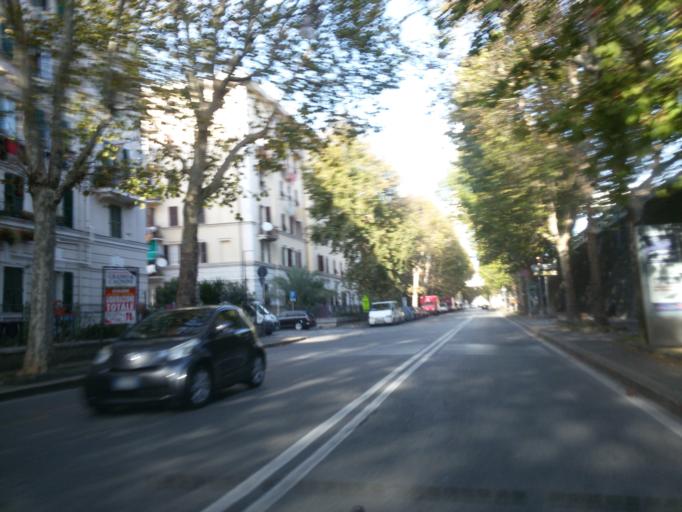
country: IT
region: Liguria
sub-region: Provincia di Genova
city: San Teodoro
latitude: 44.4230
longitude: 8.8893
